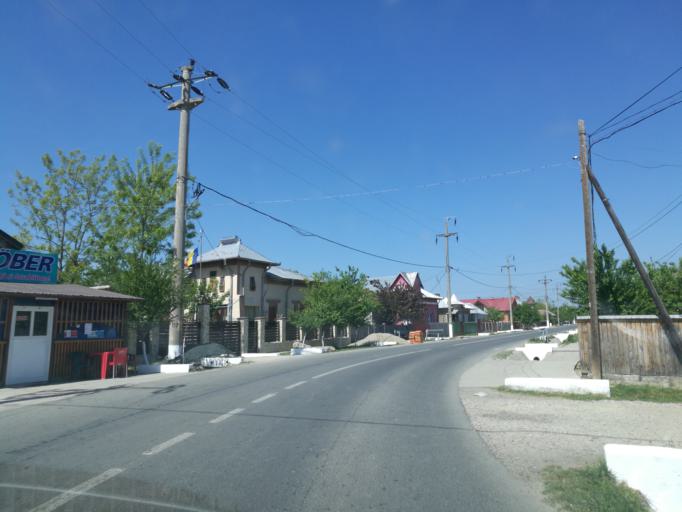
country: RO
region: Ialomita
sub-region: Comuna Adancata
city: Adancata
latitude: 44.7648
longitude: 26.4394
